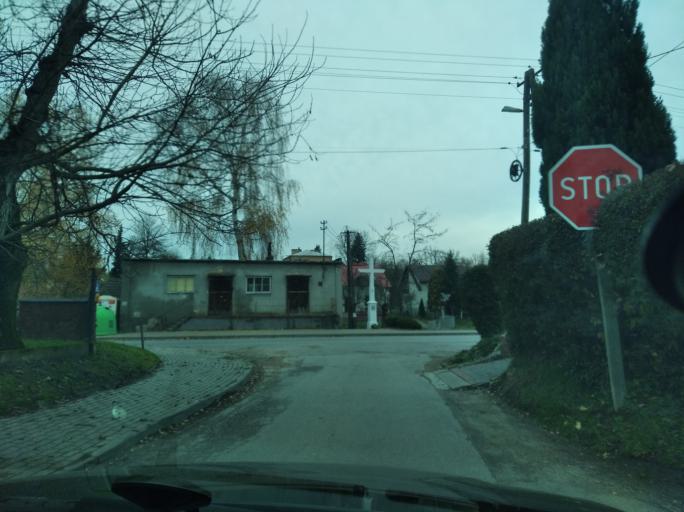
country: PL
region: Subcarpathian Voivodeship
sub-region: Powiat przeworski
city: Grzeska
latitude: 50.0754
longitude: 22.4532
